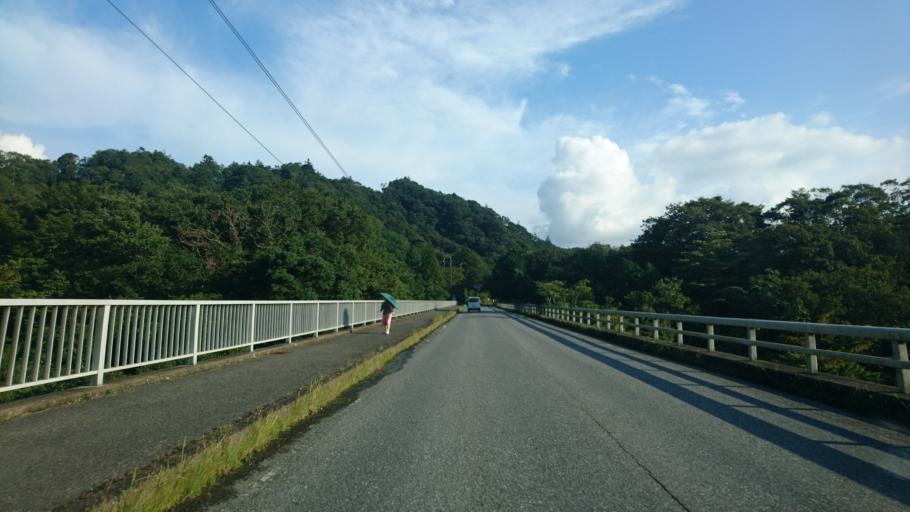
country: JP
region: Chiba
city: Kawaguchi
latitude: 35.1762
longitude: 140.0081
